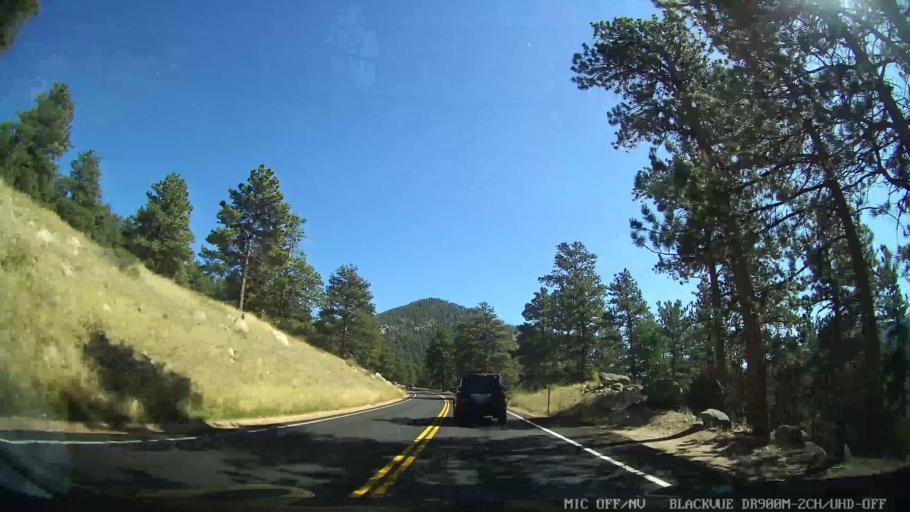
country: US
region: Colorado
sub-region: Larimer County
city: Estes Park
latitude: 40.3605
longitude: -105.5878
